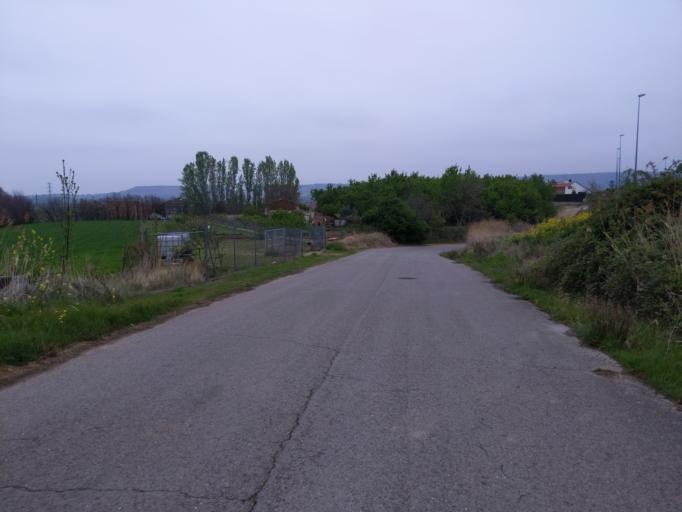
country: ES
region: La Rioja
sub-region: Provincia de La Rioja
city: Lardero
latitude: 42.4143
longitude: -2.4673
